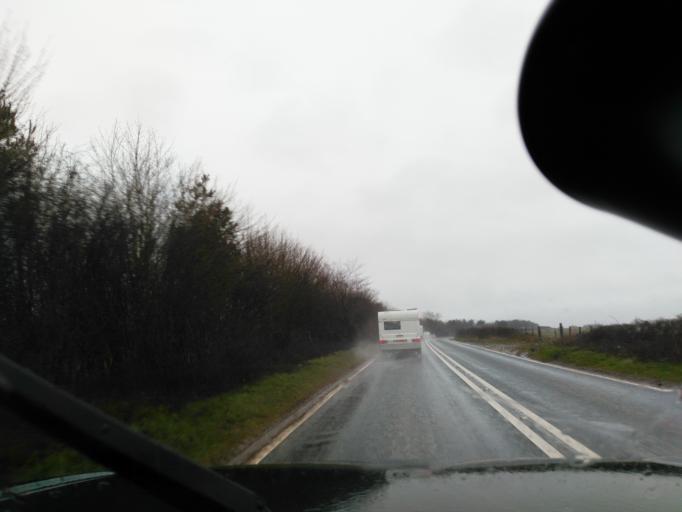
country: GB
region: England
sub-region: Somerset
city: Frome
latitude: 51.2006
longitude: -2.4049
